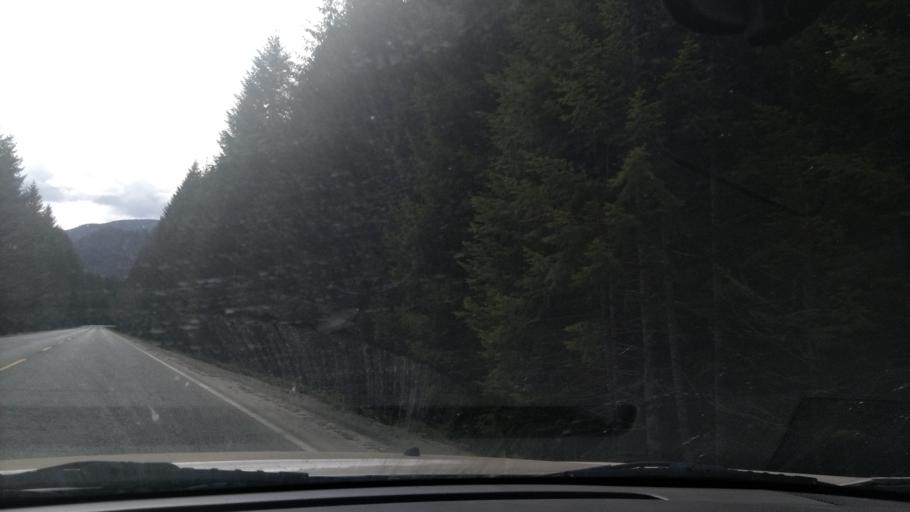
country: CA
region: British Columbia
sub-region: Regional District of Alberni-Clayoquot
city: Tofino
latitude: 49.8334
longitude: -125.9646
